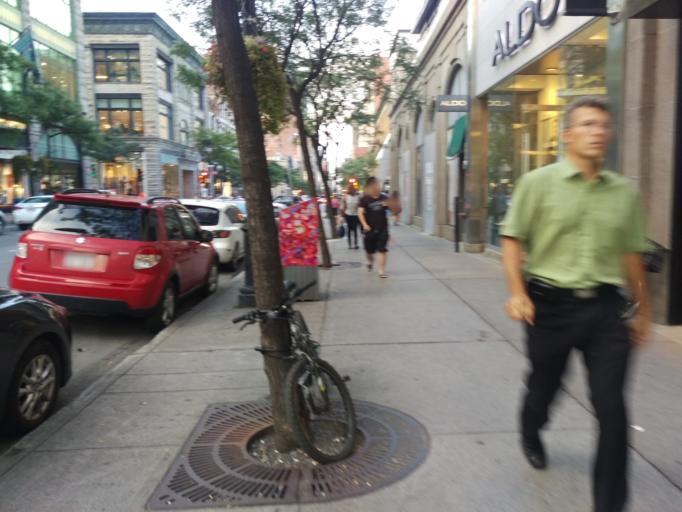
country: CA
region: Quebec
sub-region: Montreal
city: Montreal
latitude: 45.4975
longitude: -73.5755
